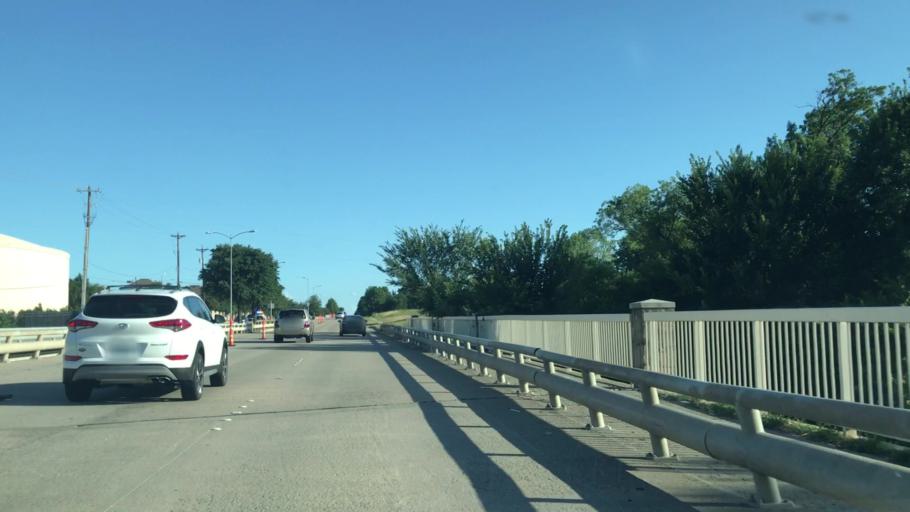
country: US
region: Texas
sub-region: Collin County
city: Allen
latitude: 33.1140
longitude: -96.7336
